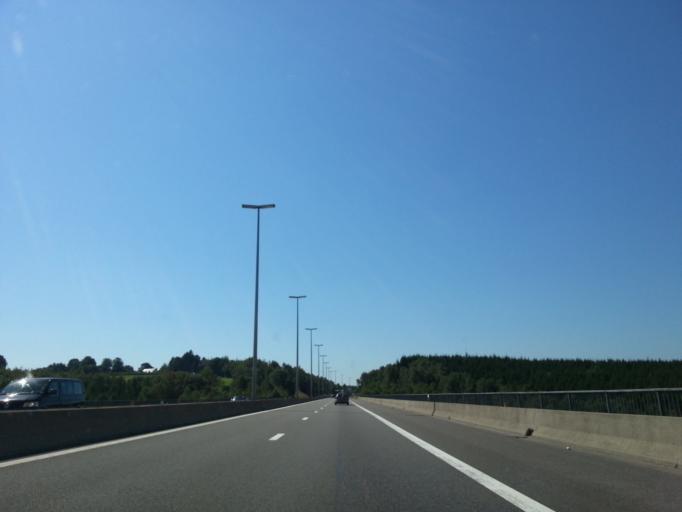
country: BE
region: Wallonia
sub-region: Province de Liege
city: Malmedy
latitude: 50.4434
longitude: 6.0074
